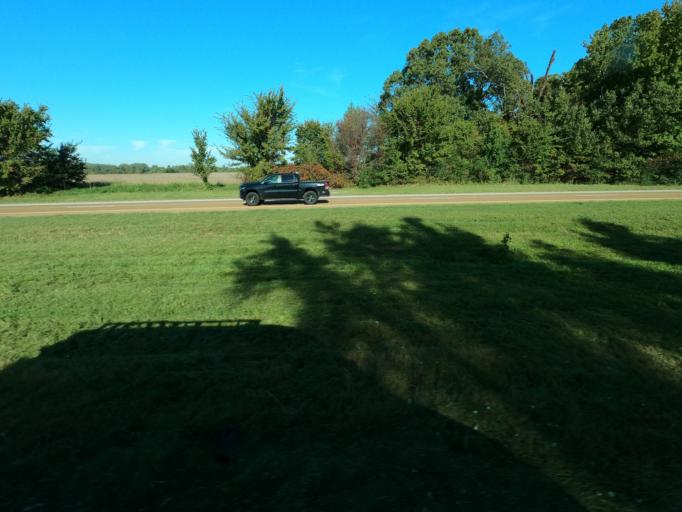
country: US
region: Tennessee
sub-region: Shelby County
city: Millington
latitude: 35.3755
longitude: -89.8748
